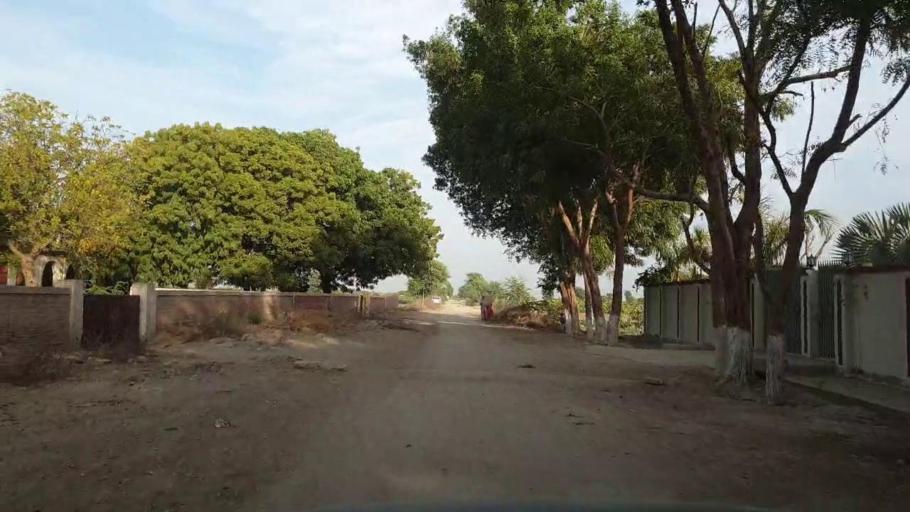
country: PK
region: Sindh
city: Kunri
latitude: 25.2272
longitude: 69.5061
